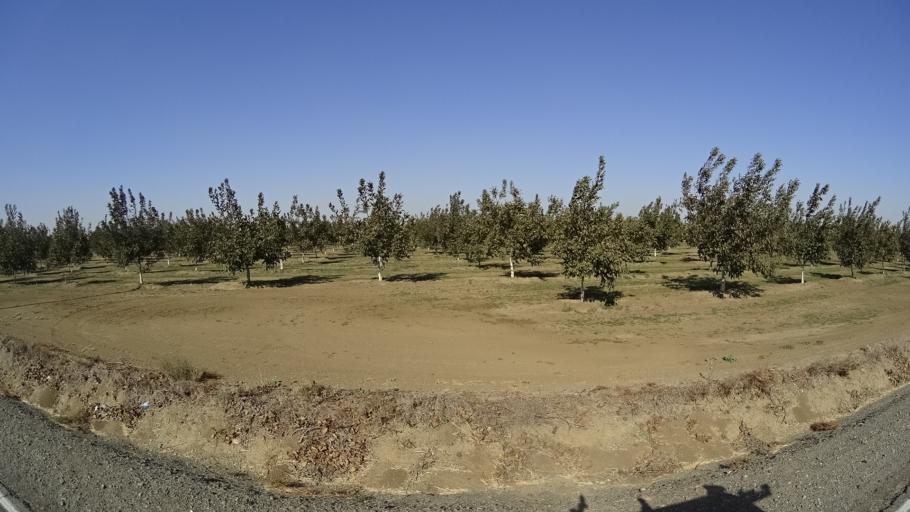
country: US
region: California
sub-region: Yolo County
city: Cottonwood
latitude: 38.7185
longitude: -121.9505
